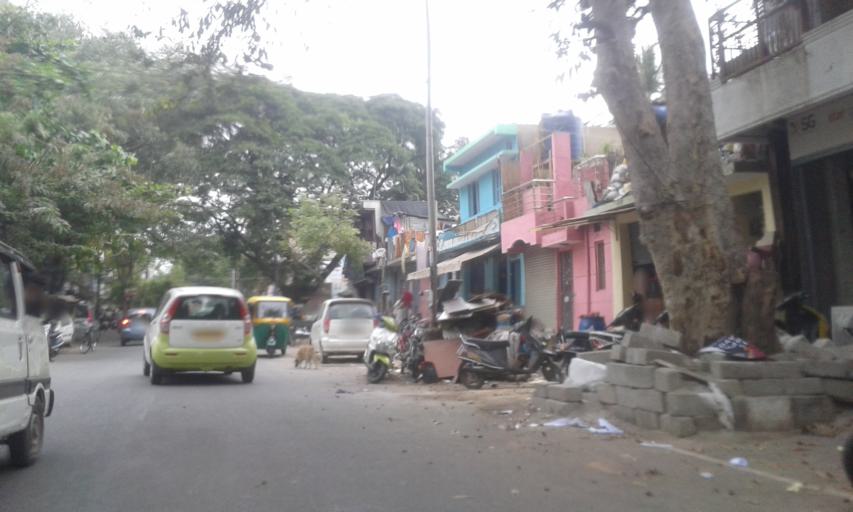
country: IN
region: Karnataka
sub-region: Bangalore Urban
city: Bangalore
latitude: 12.9205
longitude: 77.5958
